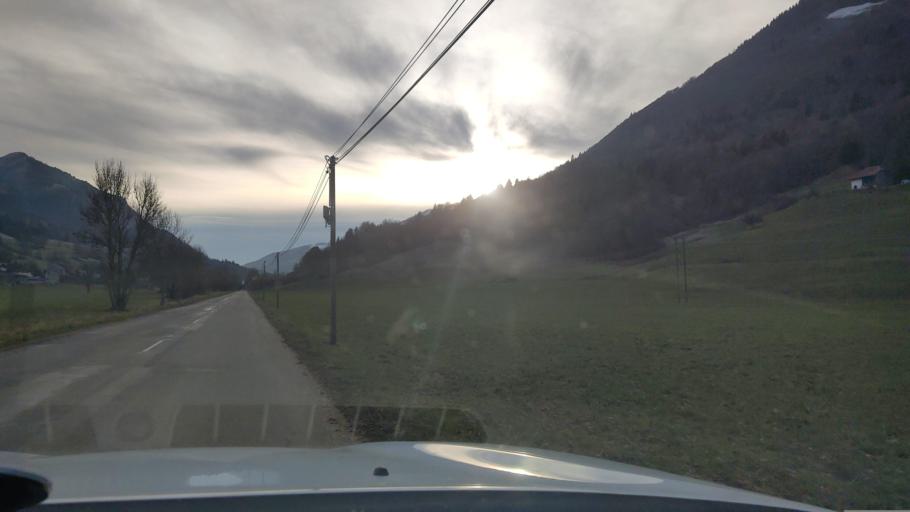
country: FR
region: Rhone-Alpes
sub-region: Departement de la Savoie
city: Gresy-sur-Isere
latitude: 45.6396
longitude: 6.1615
